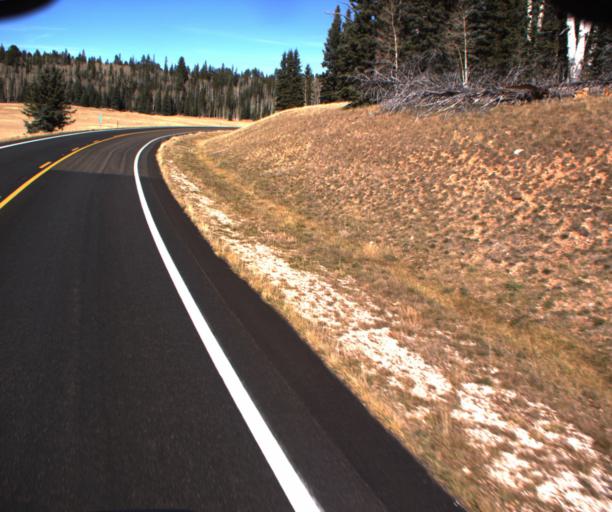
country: US
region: Arizona
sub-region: Coconino County
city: Grand Canyon
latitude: 36.4397
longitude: -112.1355
